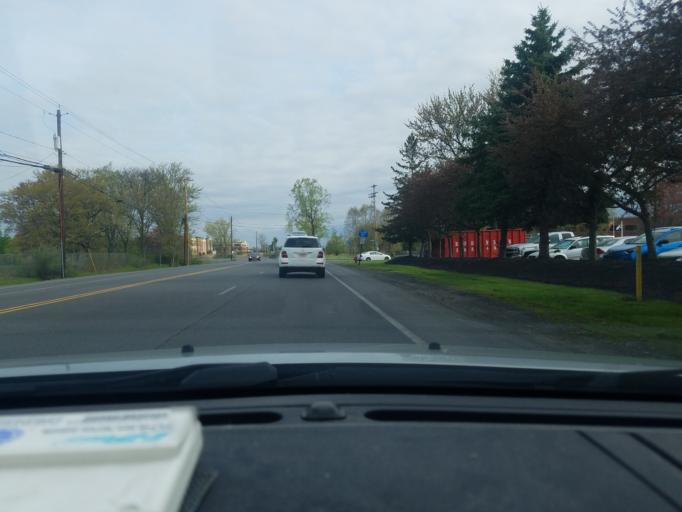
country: US
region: New York
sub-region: Onondaga County
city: East Syracuse
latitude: 43.0852
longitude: -76.0780
